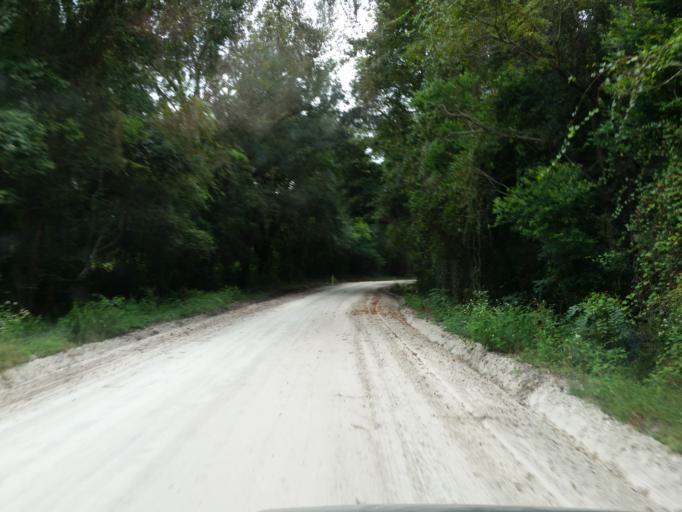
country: US
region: Florida
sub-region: Alachua County
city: High Springs
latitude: 29.9689
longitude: -82.5602
